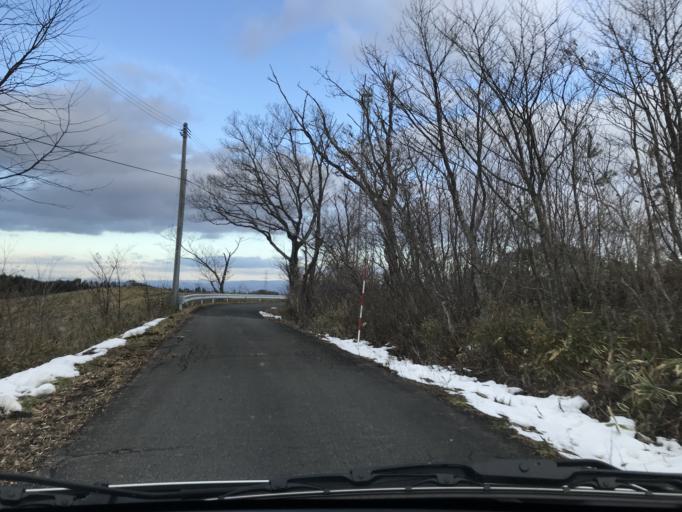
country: JP
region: Iwate
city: Ichinoseki
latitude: 38.9761
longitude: 141.0299
